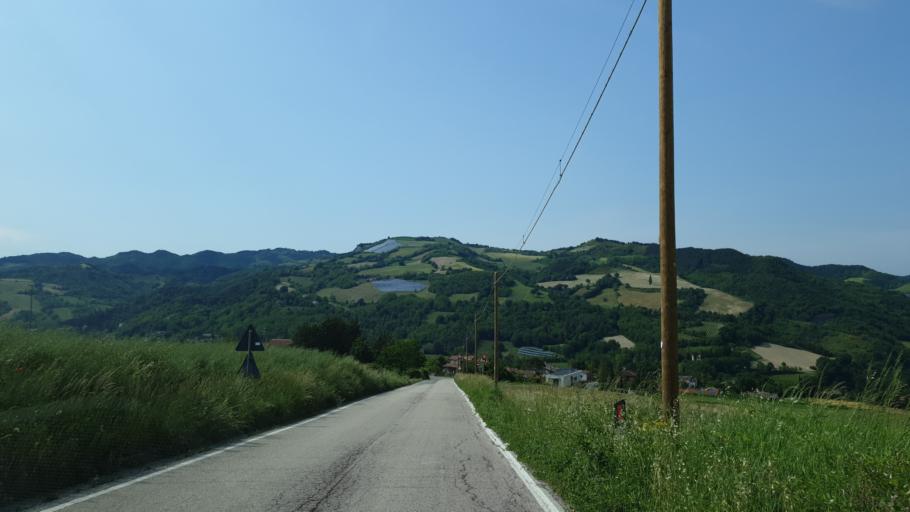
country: IT
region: Emilia-Romagna
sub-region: Forli-Cesena
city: Sarsina
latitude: 43.9170
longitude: 12.1707
